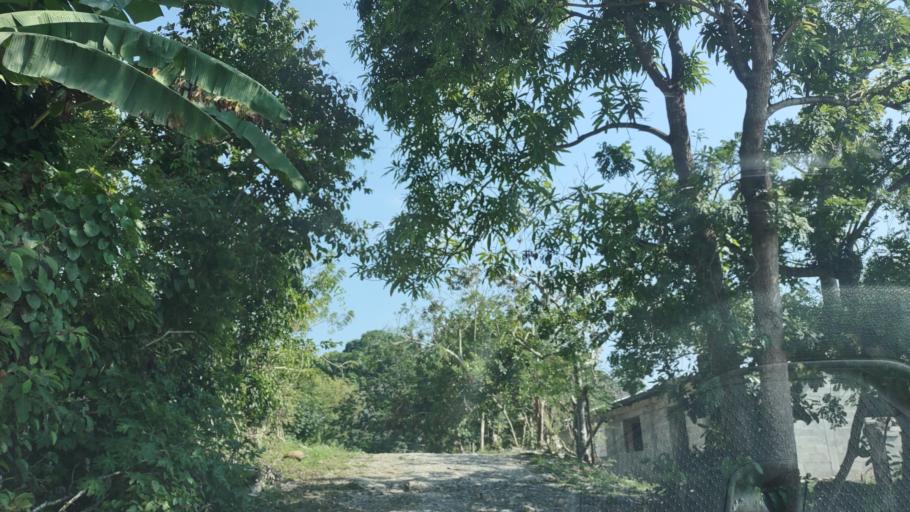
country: MX
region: Veracruz
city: Agua Dulce
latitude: 20.2946
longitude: -97.2831
